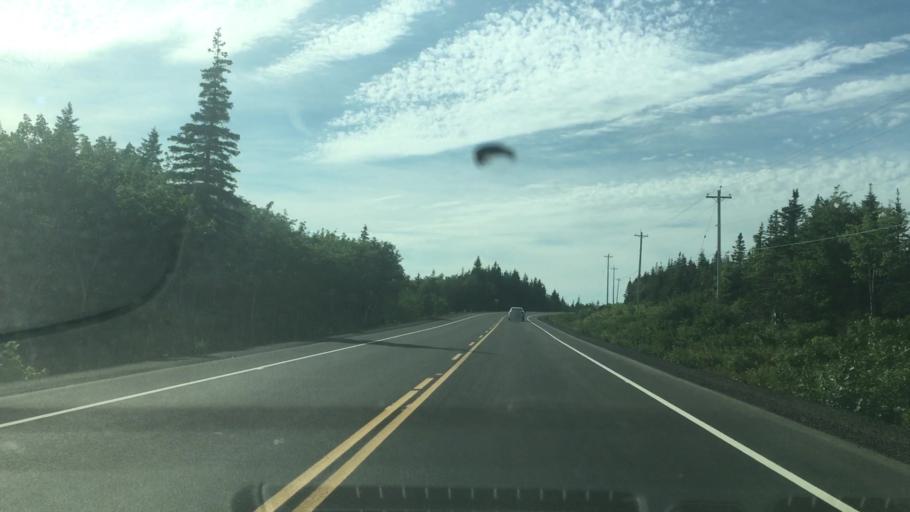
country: CA
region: Nova Scotia
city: Sydney Mines
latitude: 46.8429
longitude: -60.3998
